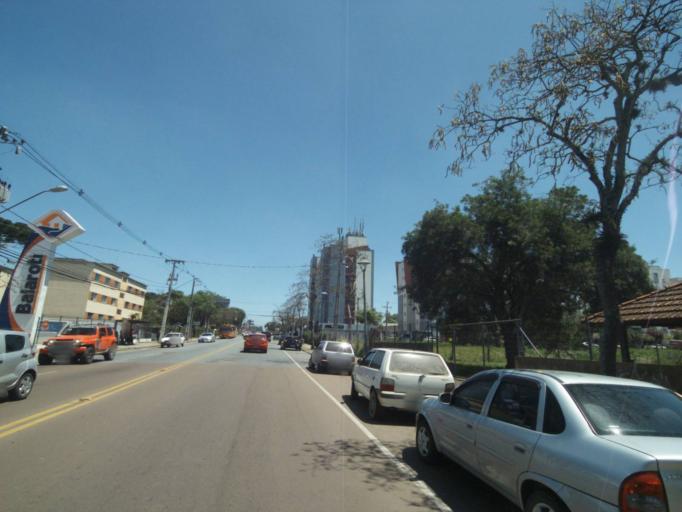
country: BR
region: Parana
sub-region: Curitiba
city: Curitiba
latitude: -25.3944
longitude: -49.2294
